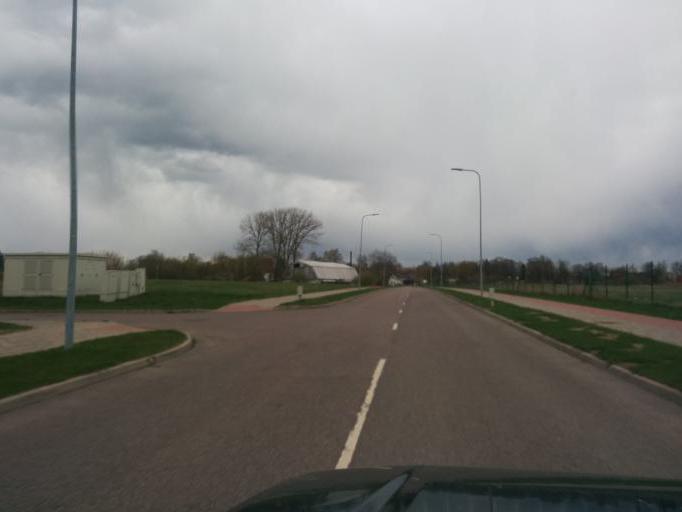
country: LV
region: Jelgava
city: Jelgava
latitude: 56.6514
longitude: 23.7405
